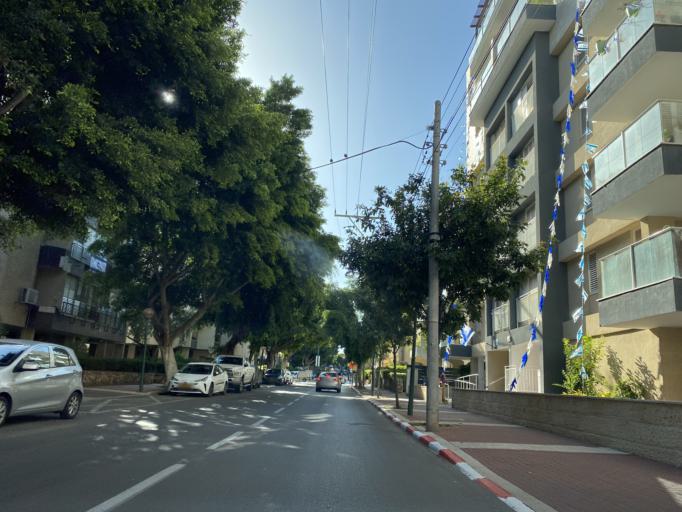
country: IL
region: Central District
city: Kfar Saba
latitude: 32.1765
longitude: 34.9161
